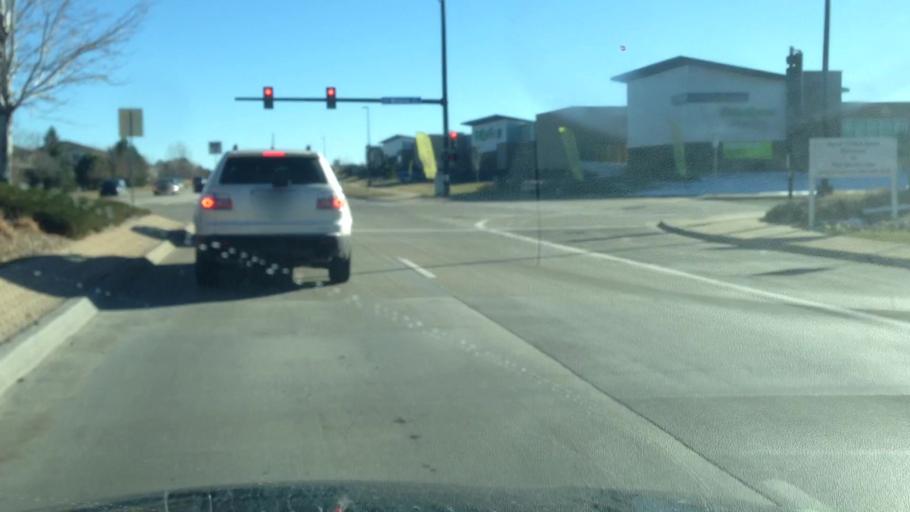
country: US
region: Colorado
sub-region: Arapahoe County
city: Dove Valley
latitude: 39.5744
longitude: -104.8064
